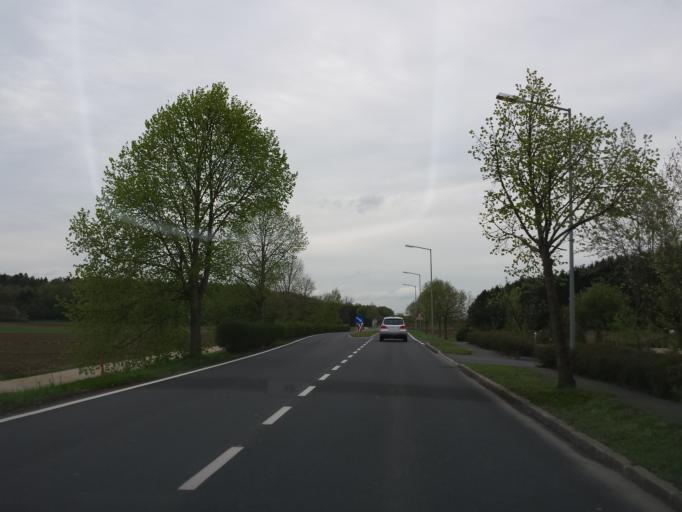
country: AT
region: Burgenland
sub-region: Politischer Bezirk Jennersdorf
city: Konigsdorf
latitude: 47.0231
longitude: 16.1492
